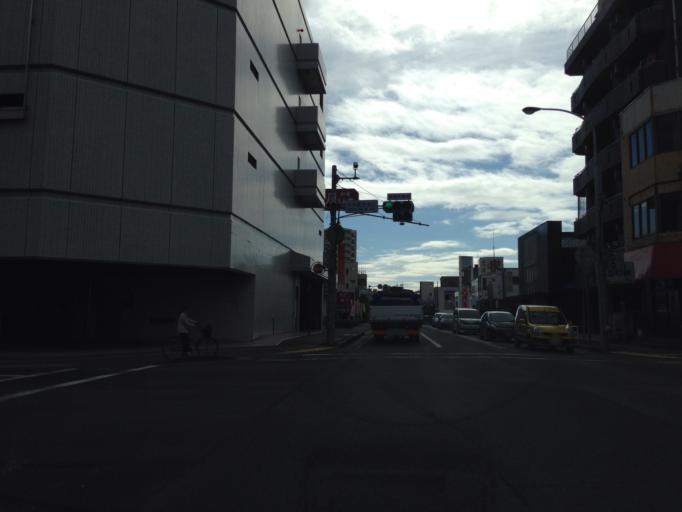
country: JP
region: Ibaraki
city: Ushiku
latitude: 35.9750
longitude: 140.1394
